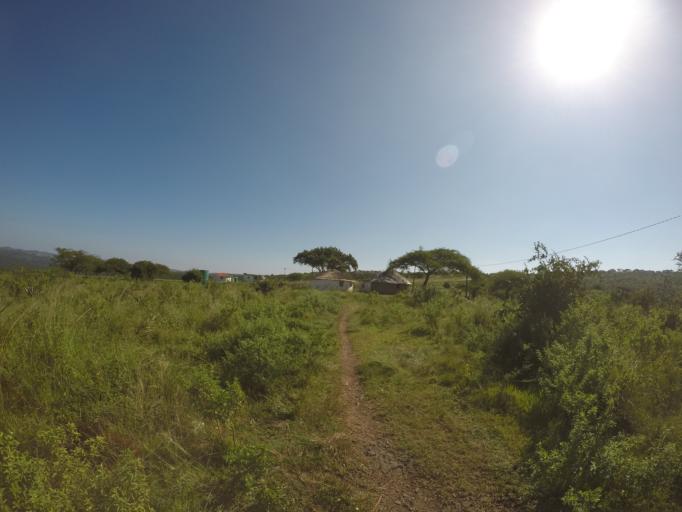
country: ZA
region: KwaZulu-Natal
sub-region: uThungulu District Municipality
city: Empangeni
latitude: -28.5706
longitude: 31.7168
